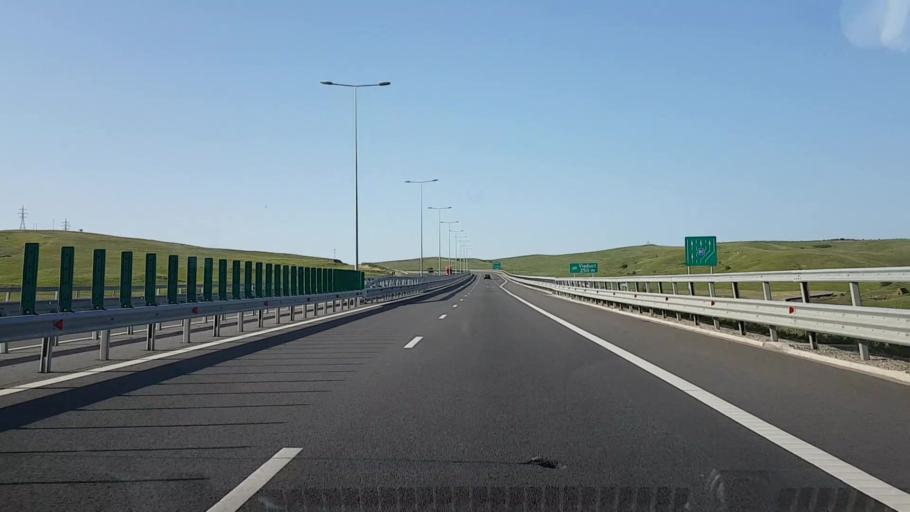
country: RO
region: Cluj
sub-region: Comuna Mihai Viteazu
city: Mihai Viteazu
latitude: 46.4876
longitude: 23.7775
